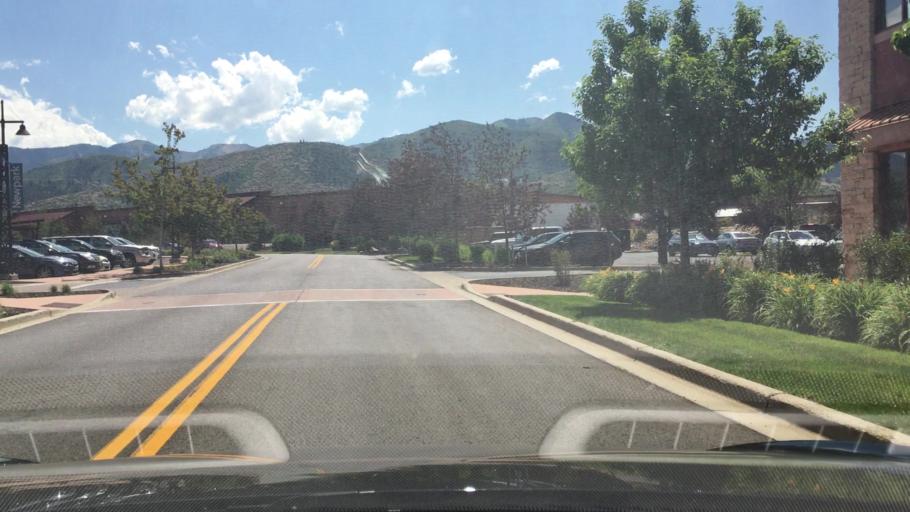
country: US
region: Utah
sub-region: Summit County
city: Snyderville
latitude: 40.7239
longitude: -111.5390
